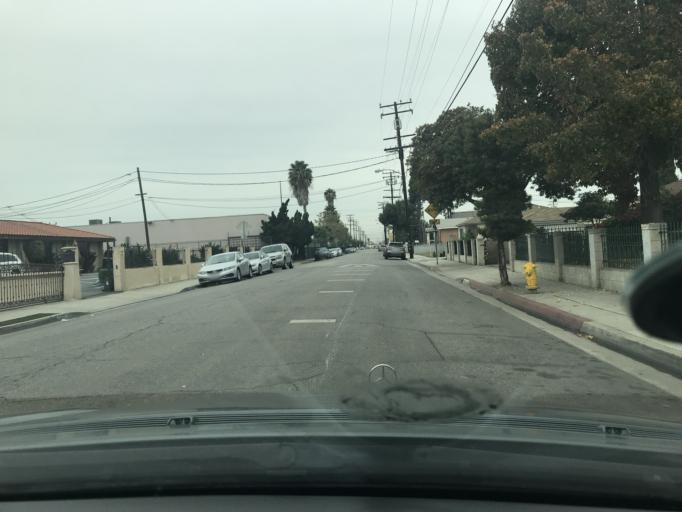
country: US
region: California
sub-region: Los Angeles County
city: Cudahy
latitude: 33.9577
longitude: -118.1773
